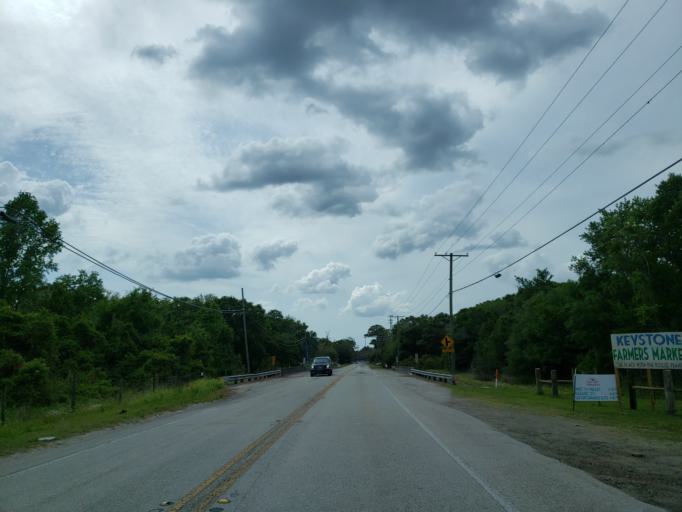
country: US
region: Florida
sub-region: Hillsborough County
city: Keystone
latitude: 28.1407
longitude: -82.6388
